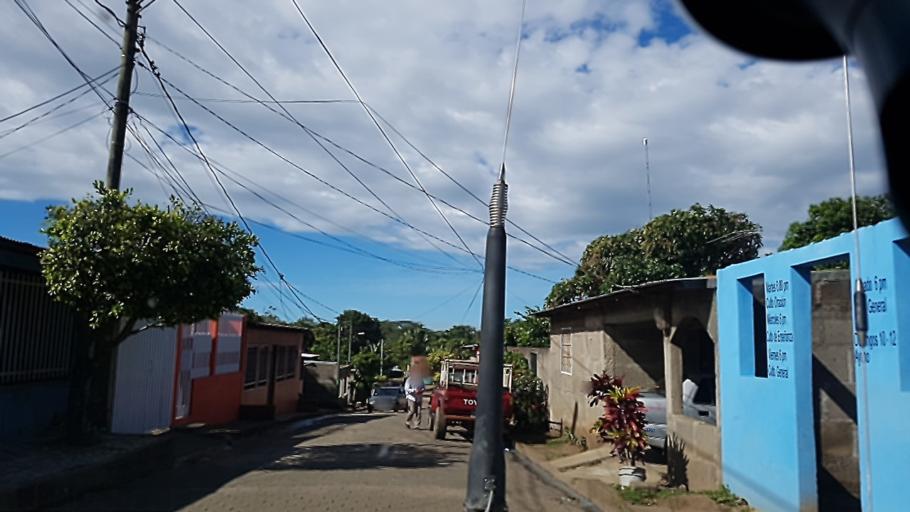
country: NI
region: Carazo
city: Dolores
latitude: 11.8574
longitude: -86.2169
